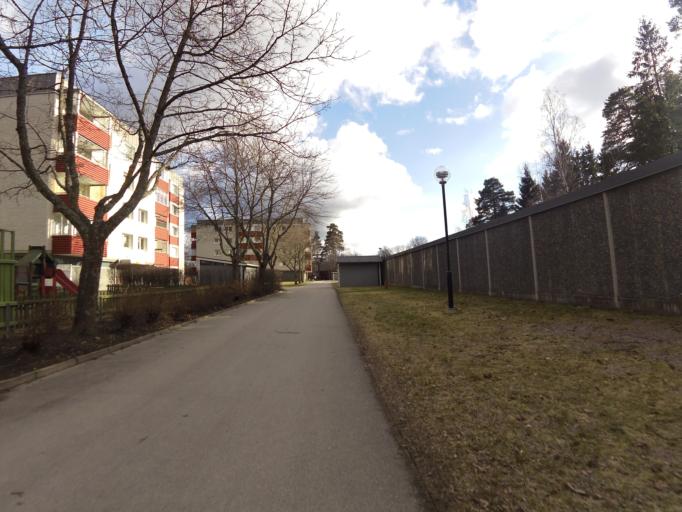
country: SE
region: Gaevleborg
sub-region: Gavle Kommun
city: Gavle
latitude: 60.6873
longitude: 17.1133
